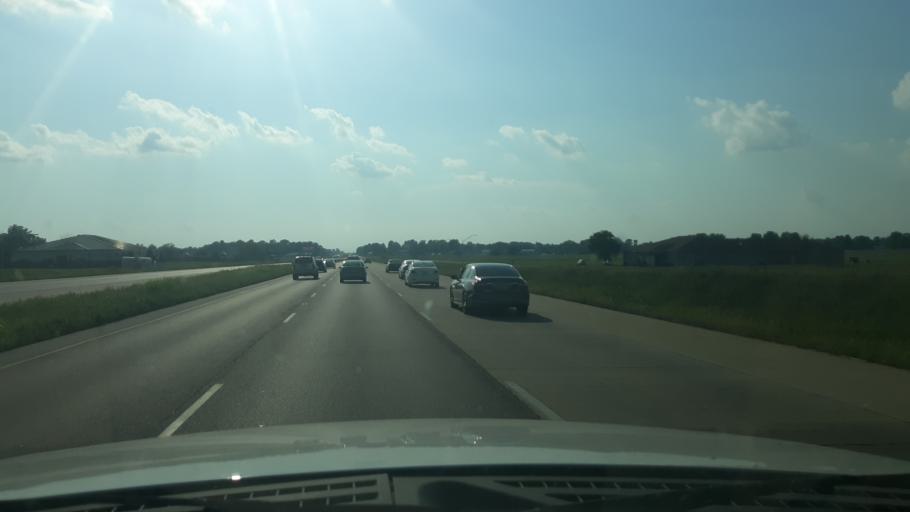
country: US
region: Illinois
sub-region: Williamson County
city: Energy
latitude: 37.7451
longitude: -89.0116
